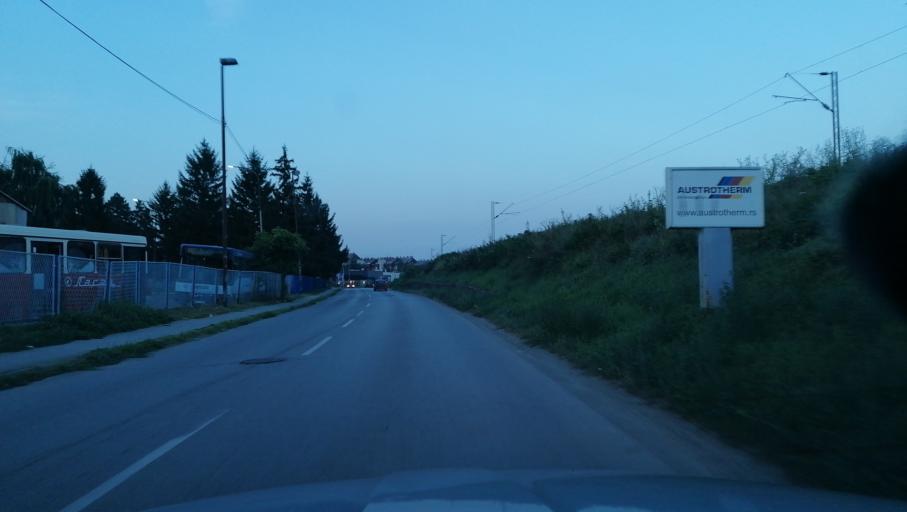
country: RS
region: Central Serbia
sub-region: Kolubarski Okrug
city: Valjevo
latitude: 44.2673
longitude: 19.8962
